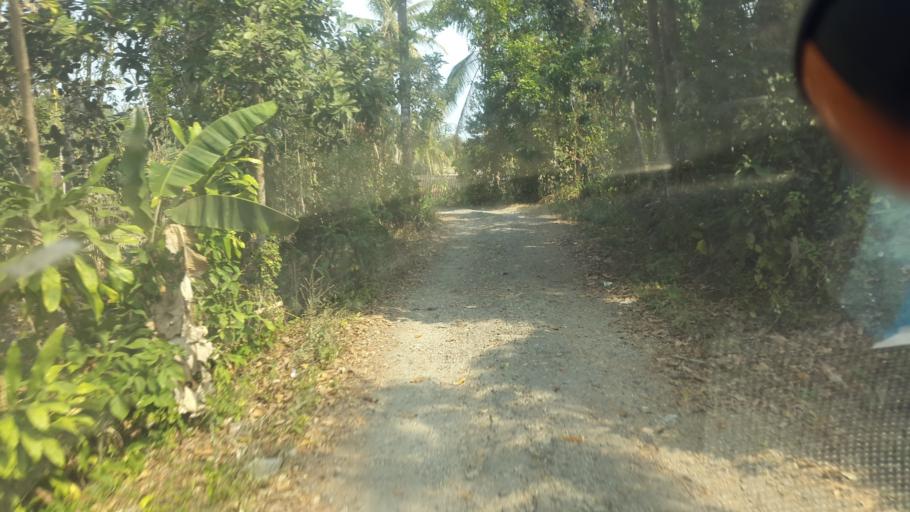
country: ID
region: West Java
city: Cinangka
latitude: -7.3207
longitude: 106.6312
